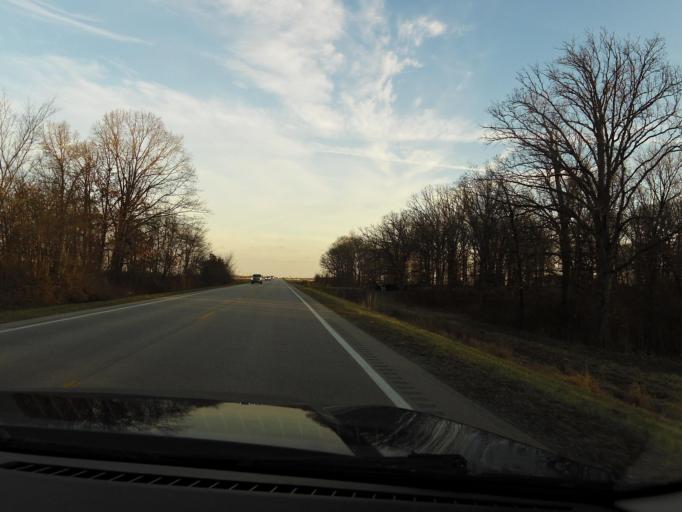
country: US
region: Illinois
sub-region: Fayette County
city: Vandalia
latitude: 38.8258
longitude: -89.0880
